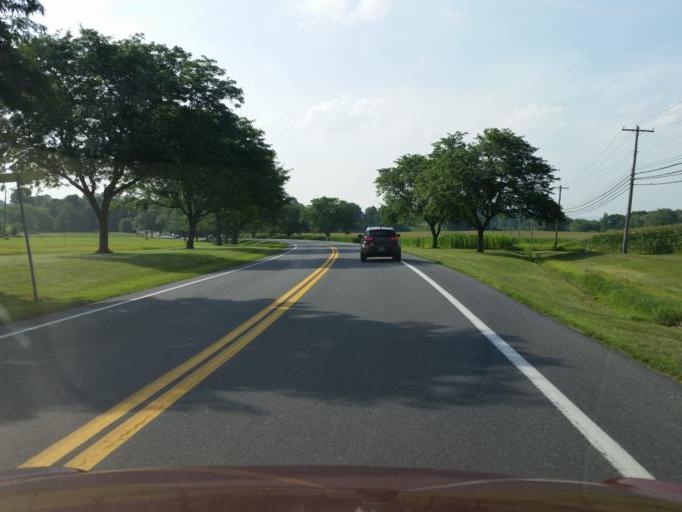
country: US
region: Pennsylvania
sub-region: Dauphin County
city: Hershey
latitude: 40.2534
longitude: -76.6283
